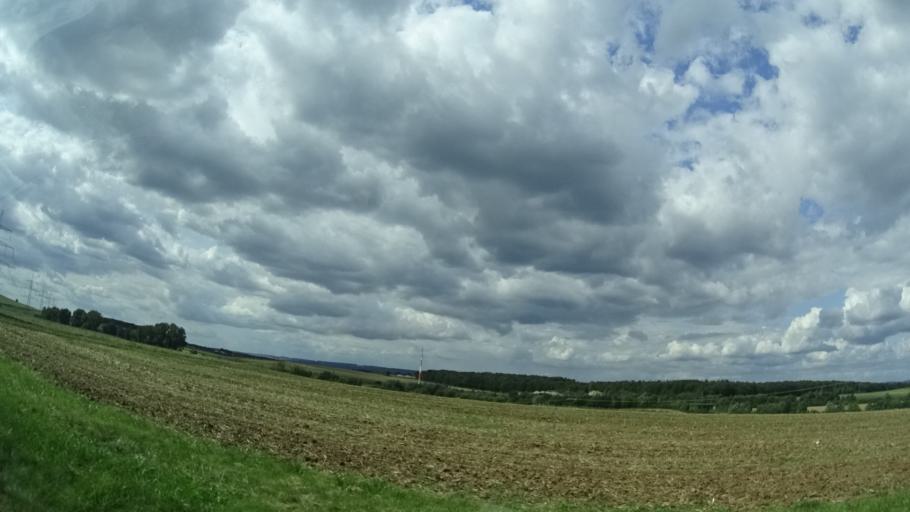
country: DE
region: Bavaria
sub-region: Regierungsbezirk Unterfranken
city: Knetzgau
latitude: 49.9870
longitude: 10.5281
